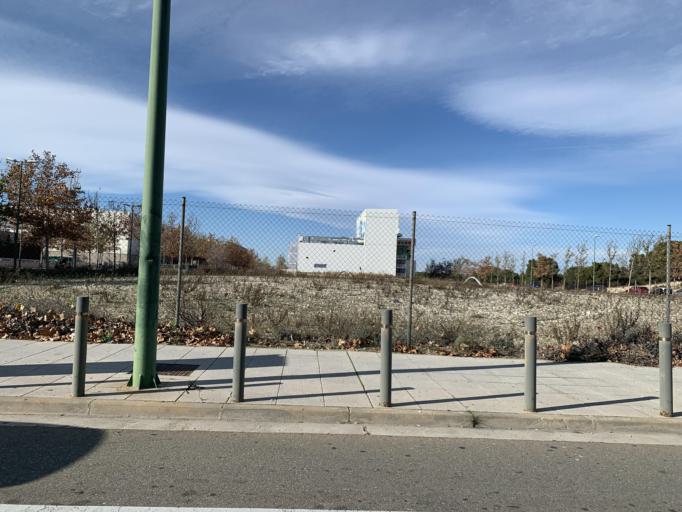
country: ES
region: Aragon
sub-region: Provincia de Zaragoza
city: Delicias
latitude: 41.6105
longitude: -0.8868
